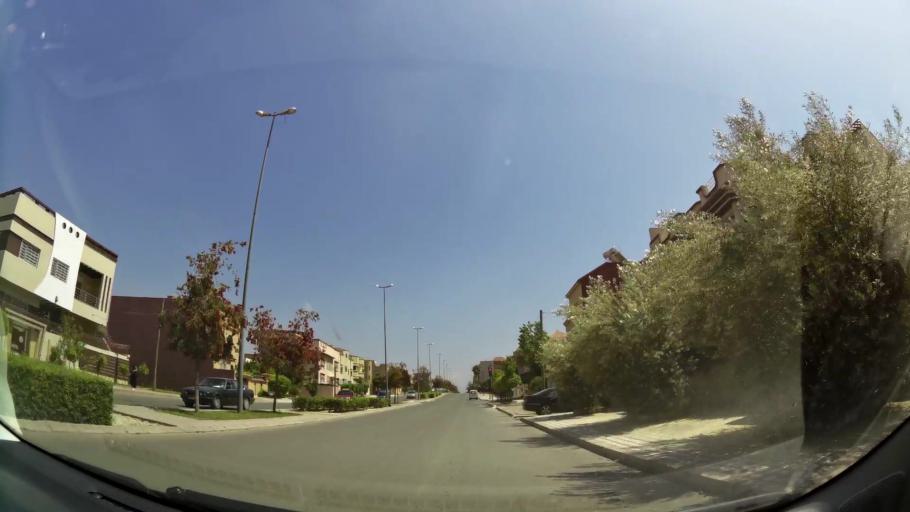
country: MA
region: Oriental
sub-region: Oujda-Angad
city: Oujda
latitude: 34.6931
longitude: -1.8803
